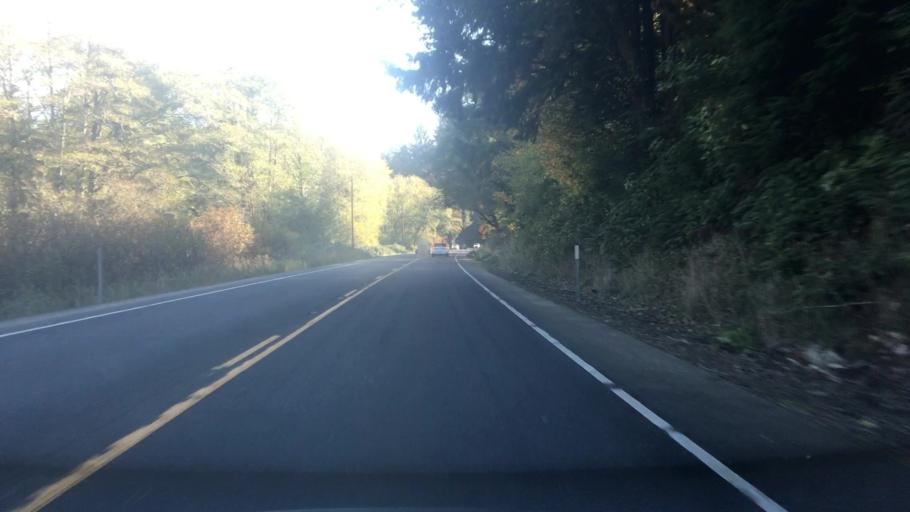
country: US
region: Oregon
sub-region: Lincoln County
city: Rose Lodge
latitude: 45.0101
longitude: -123.9226
